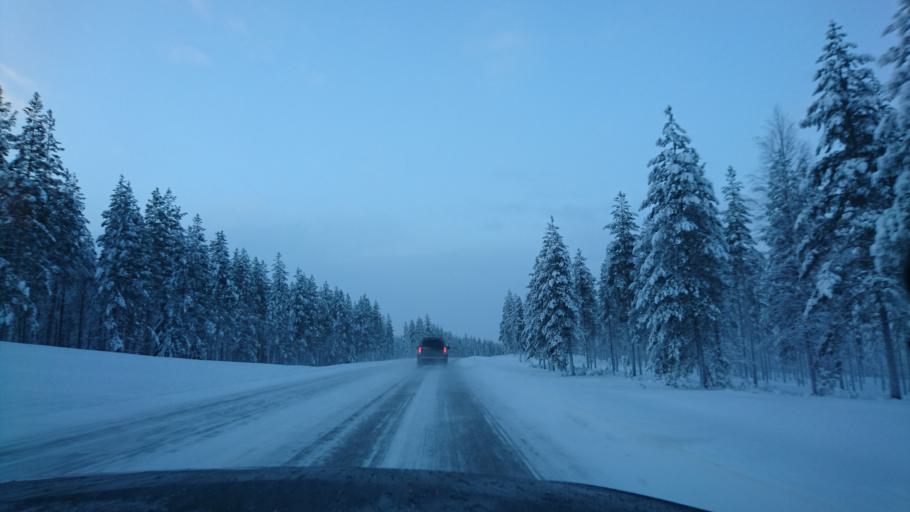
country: FI
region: Northern Ostrobothnia
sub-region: Koillismaa
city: Taivalkoski
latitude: 65.4689
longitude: 27.7236
